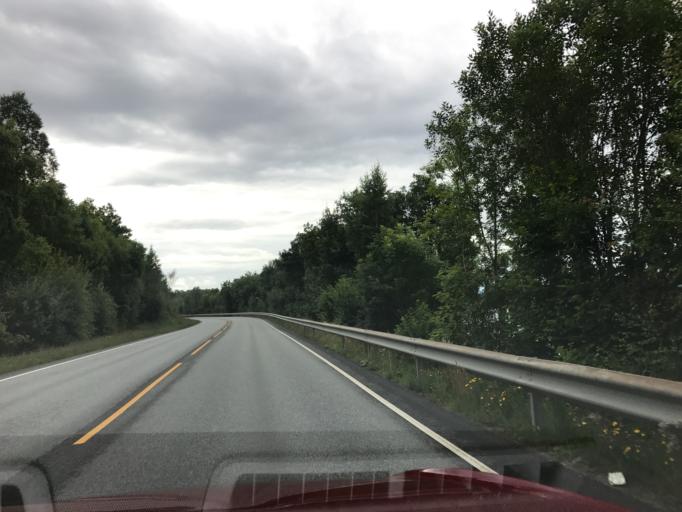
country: NO
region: Rogaland
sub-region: Strand
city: Tau
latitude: 59.0295
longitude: 5.9473
